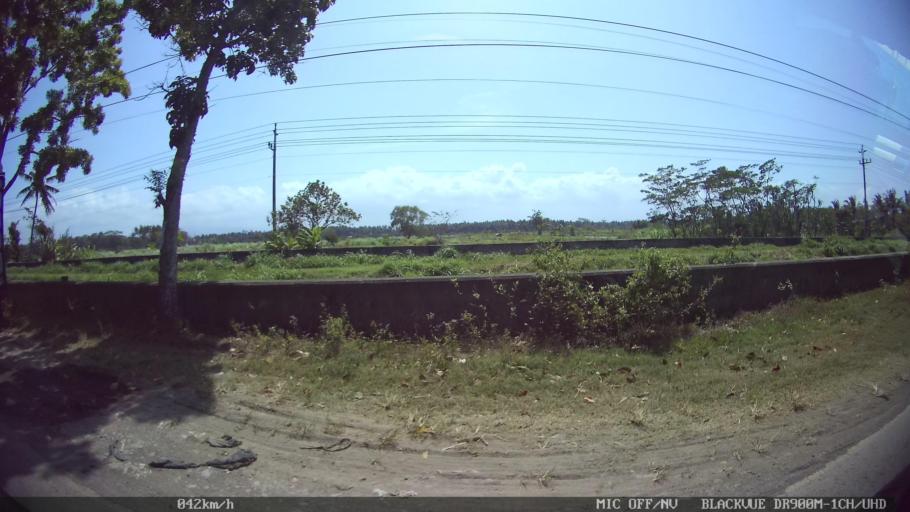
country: ID
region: Daerah Istimewa Yogyakarta
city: Srandakan
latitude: -7.9317
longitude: 110.1415
